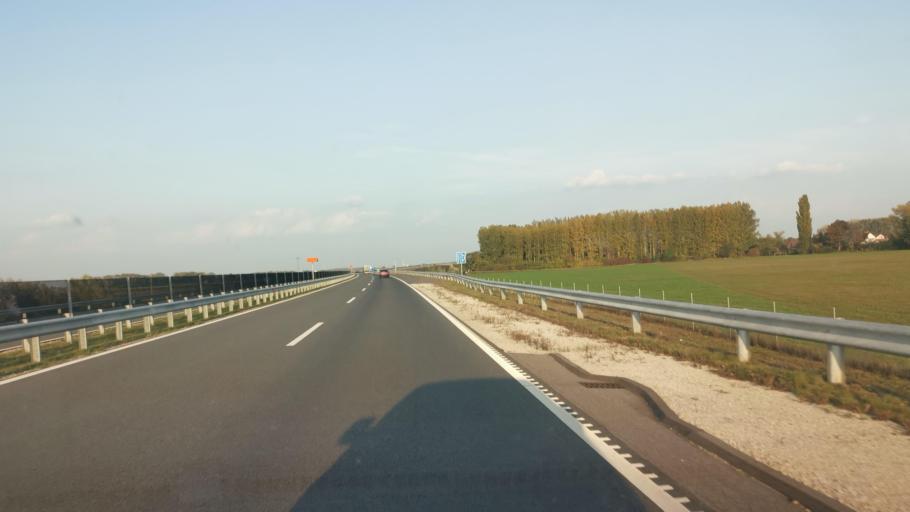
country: HU
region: Gyor-Moson-Sopron
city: Farad
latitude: 47.5861
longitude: 17.1814
